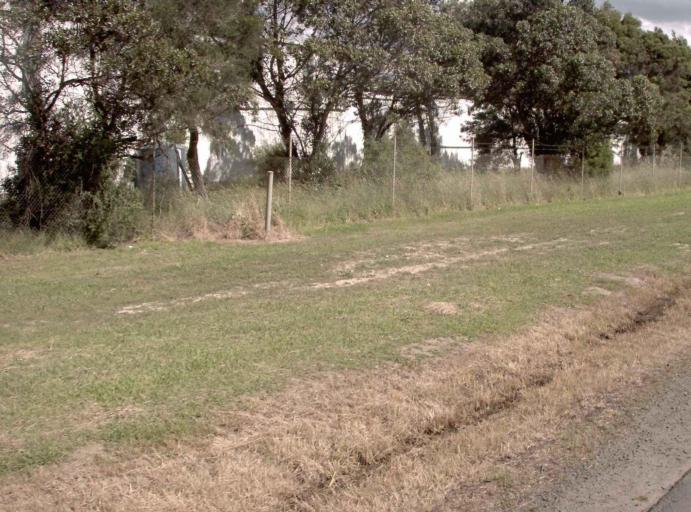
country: AU
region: Victoria
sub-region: Latrobe
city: Morwell
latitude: -38.2496
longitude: 146.4358
